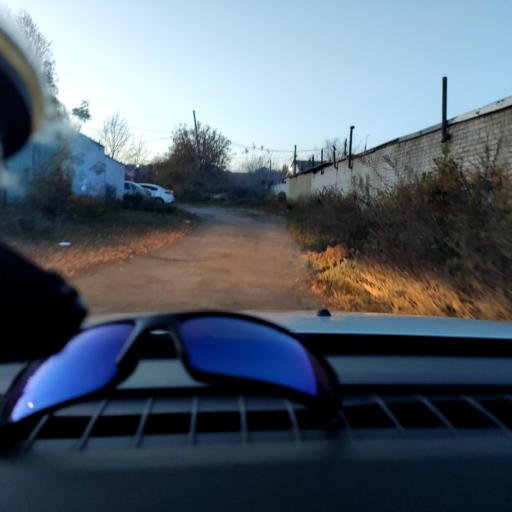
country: RU
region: Samara
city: Samara
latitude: 53.2269
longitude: 50.2234
